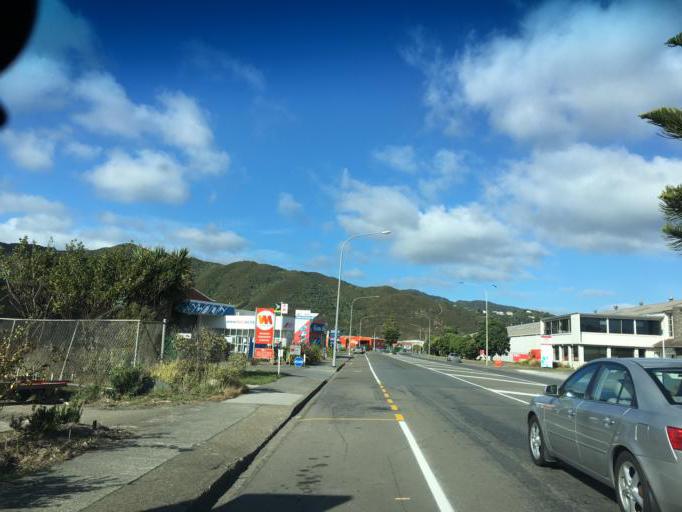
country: NZ
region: Wellington
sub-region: Lower Hutt City
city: Lower Hutt
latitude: -41.2377
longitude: 174.9069
